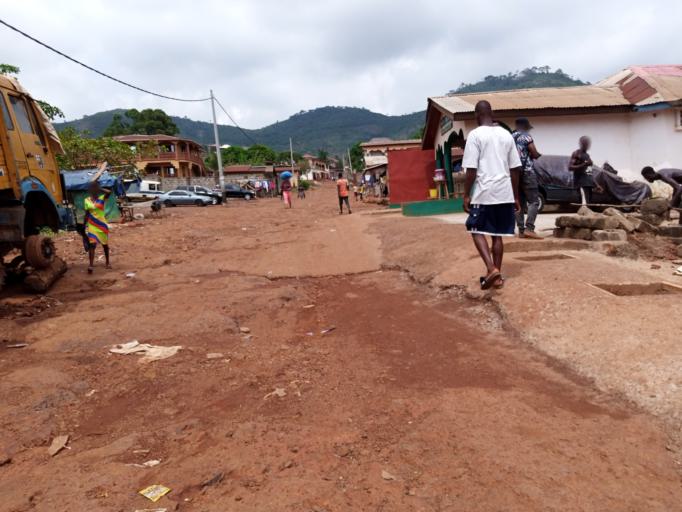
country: SL
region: Western Area
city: Waterloo
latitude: 8.3680
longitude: -13.0927
